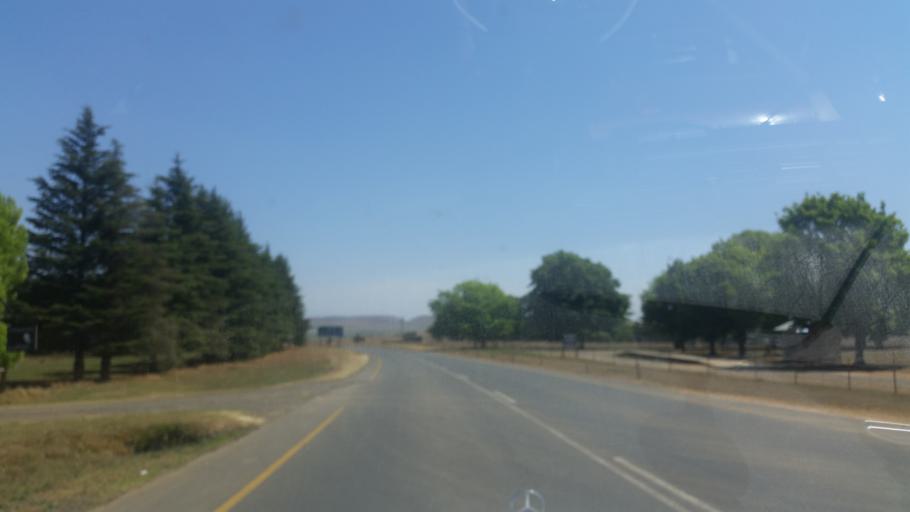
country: ZA
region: KwaZulu-Natal
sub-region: uMgungundlovu District Municipality
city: Mooirivier
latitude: -29.1483
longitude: 29.9761
